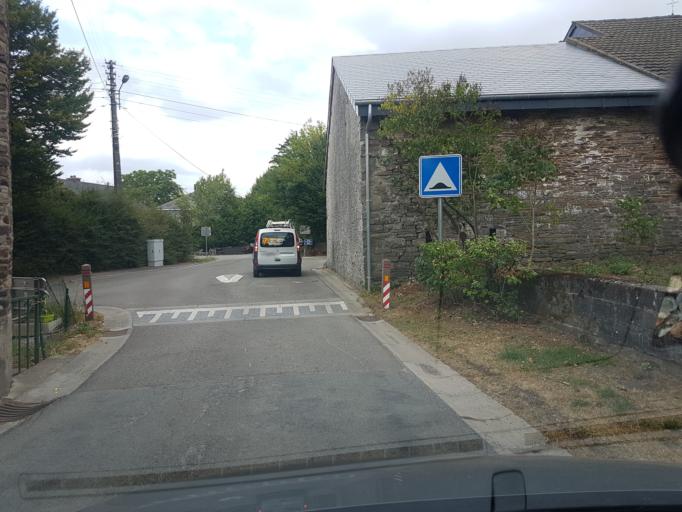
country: BE
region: Wallonia
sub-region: Province du Luxembourg
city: Manhay
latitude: 50.2565
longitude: 5.6493
